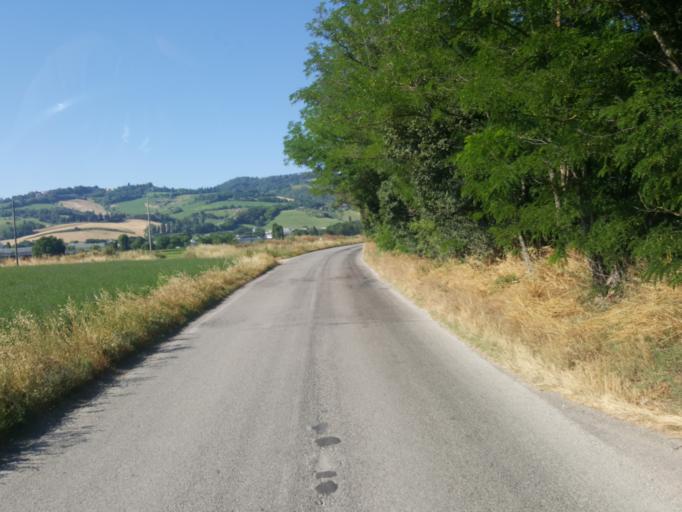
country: IT
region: The Marches
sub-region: Provincia di Pesaro e Urbino
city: Padiglione
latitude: 43.8425
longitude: 12.7196
